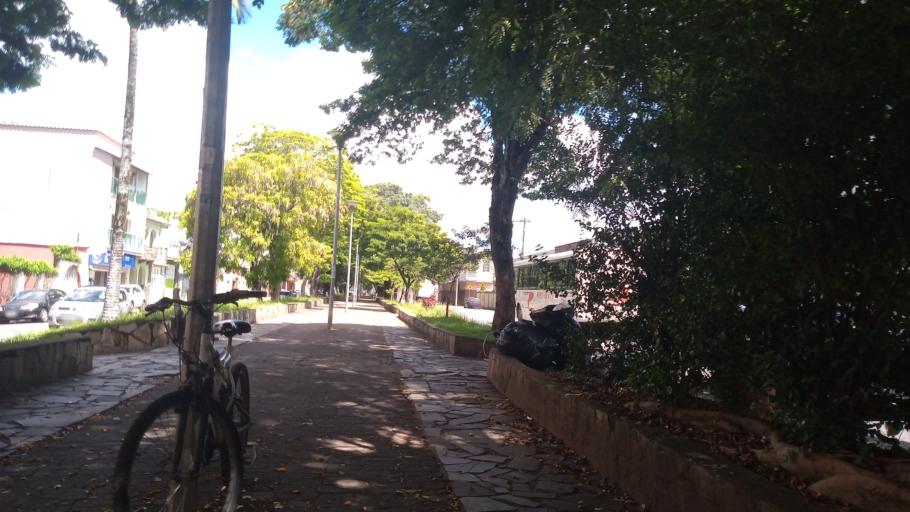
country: BR
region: Minas Gerais
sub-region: Sao Joao Del Rei
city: Sao Joao del Rei
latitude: -21.1286
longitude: -44.2499
